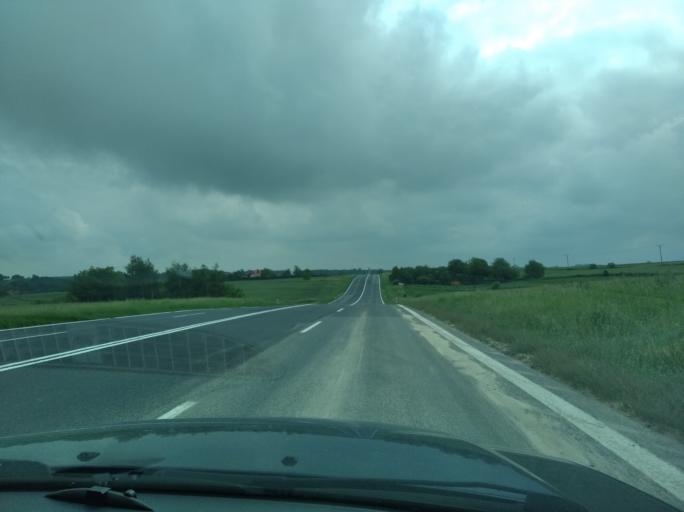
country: PL
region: Subcarpathian Voivodeship
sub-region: Powiat przeworski
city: Rozborz
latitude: 50.0481
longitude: 22.5350
